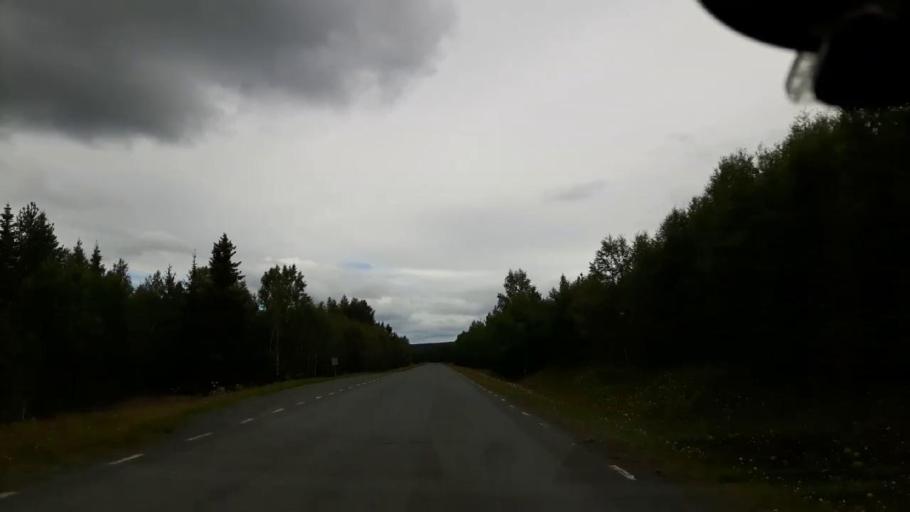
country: SE
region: Jaemtland
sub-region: Krokoms Kommun
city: Valla
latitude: 63.6314
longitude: 13.8168
